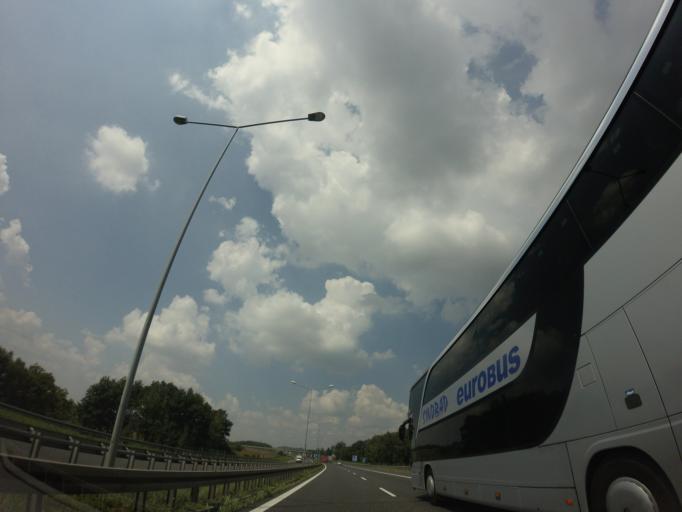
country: PL
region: Silesian Voivodeship
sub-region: Powiat gliwicki
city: Rudziniec
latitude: 50.3887
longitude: 18.4549
